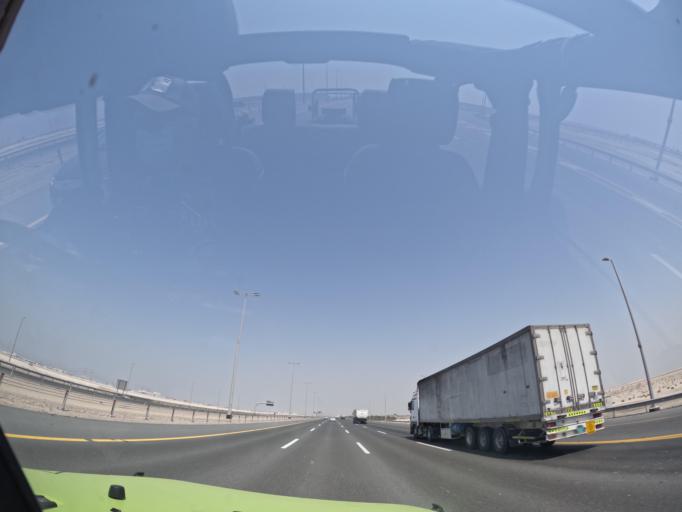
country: AE
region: Abu Dhabi
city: Abu Dhabi
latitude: 24.2509
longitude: 54.4780
